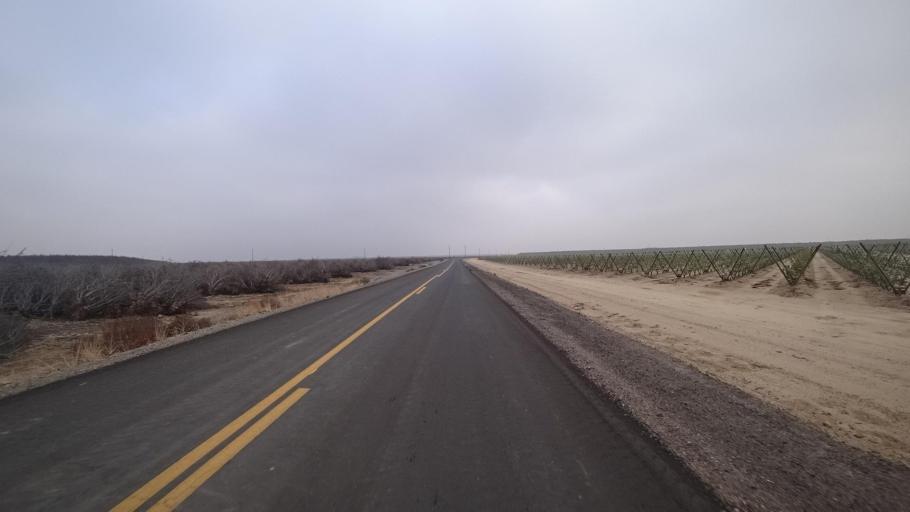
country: US
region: California
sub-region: Kern County
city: Maricopa
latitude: 35.1156
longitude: -119.3537
